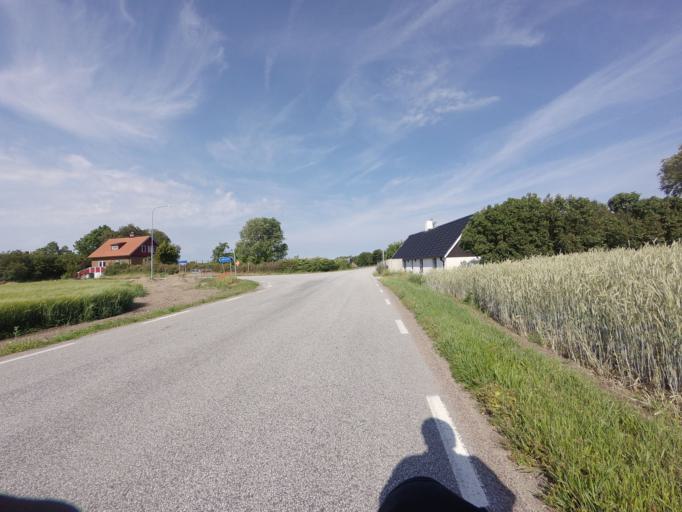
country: SE
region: Skane
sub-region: Malmo
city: Oxie
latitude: 55.4947
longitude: 13.0830
